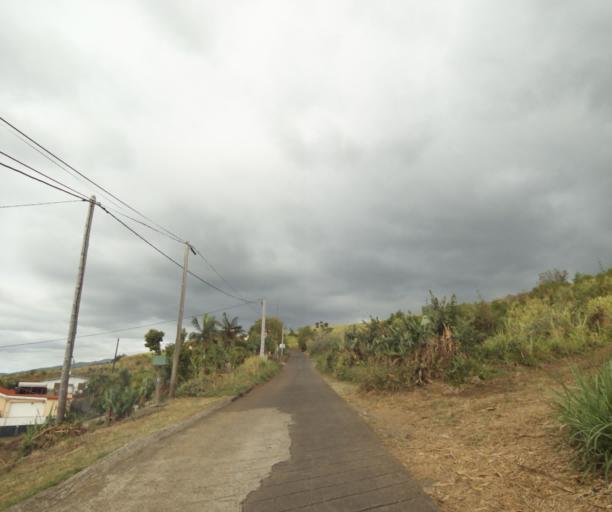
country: RE
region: Reunion
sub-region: Reunion
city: Saint-Paul
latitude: -21.0306
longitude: 55.3137
